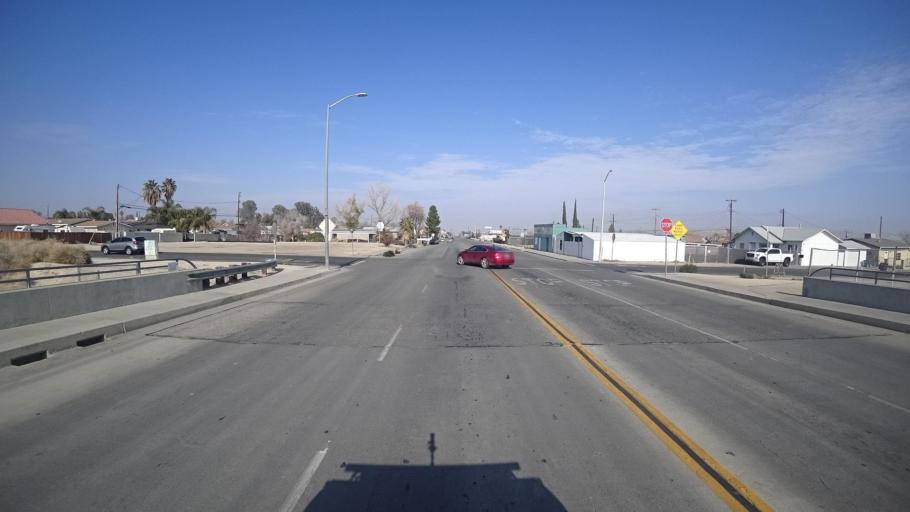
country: US
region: California
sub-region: Kern County
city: Ford City
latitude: 35.1512
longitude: -119.4564
